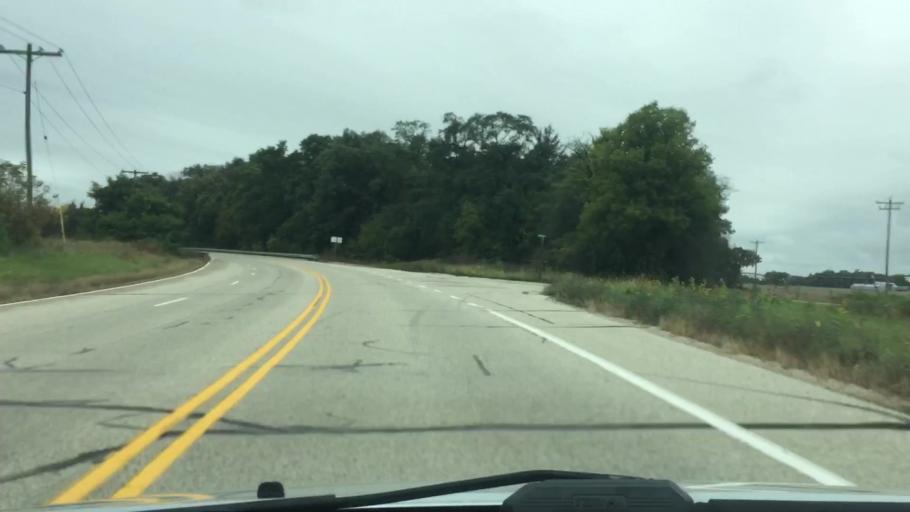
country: US
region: Wisconsin
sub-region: Jefferson County
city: Palmyra
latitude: 42.8176
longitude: -88.5619
